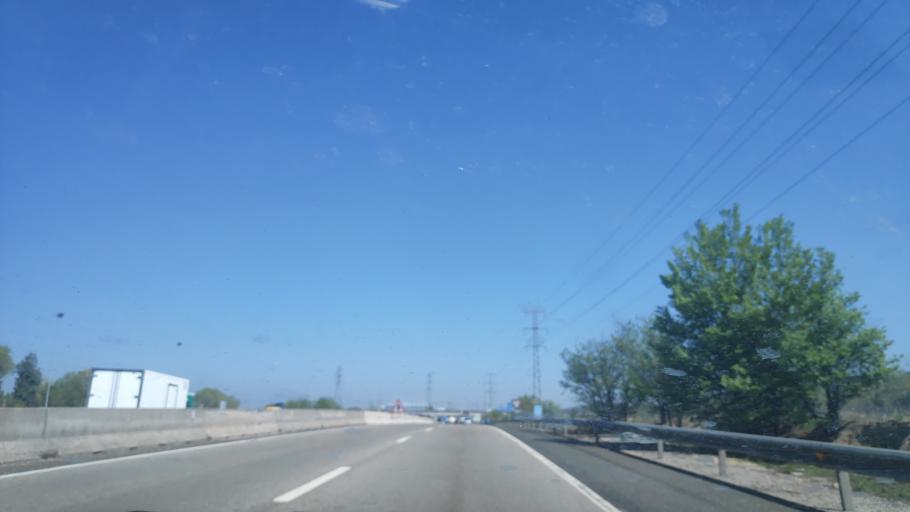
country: ES
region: Madrid
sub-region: Provincia de Madrid
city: Pinto
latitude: 40.2815
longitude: -3.6906
